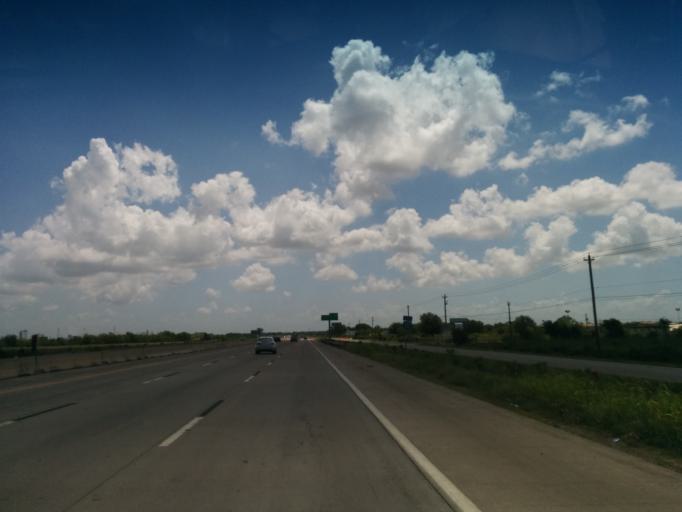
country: US
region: Texas
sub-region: Chambers County
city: Mont Belvieu
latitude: 29.8092
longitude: -94.9563
